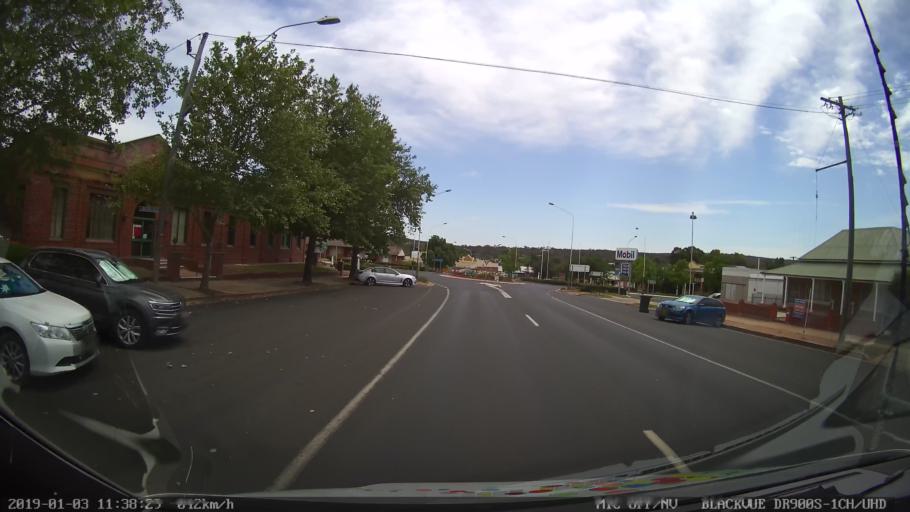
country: AU
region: New South Wales
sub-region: Weddin
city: Grenfell
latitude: -33.8959
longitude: 148.1626
